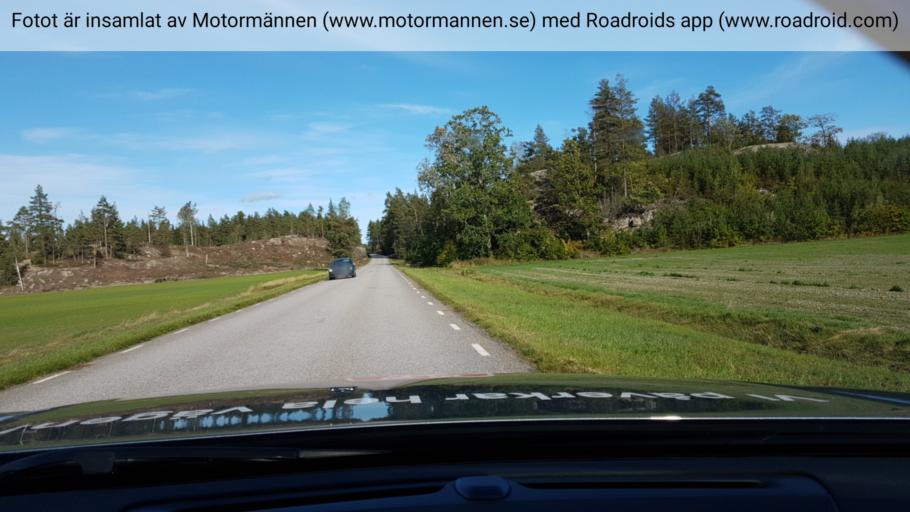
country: SE
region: OEstergoetland
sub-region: Valdemarsviks Kommun
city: Valdemarsvik
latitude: 58.0600
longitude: 16.6287
